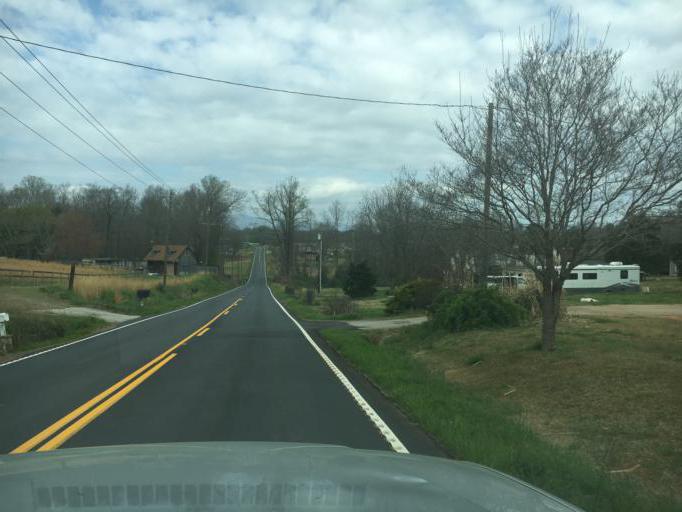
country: US
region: South Carolina
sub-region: Spartanburg County
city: Landrum
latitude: 35.0825
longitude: -82.1894
